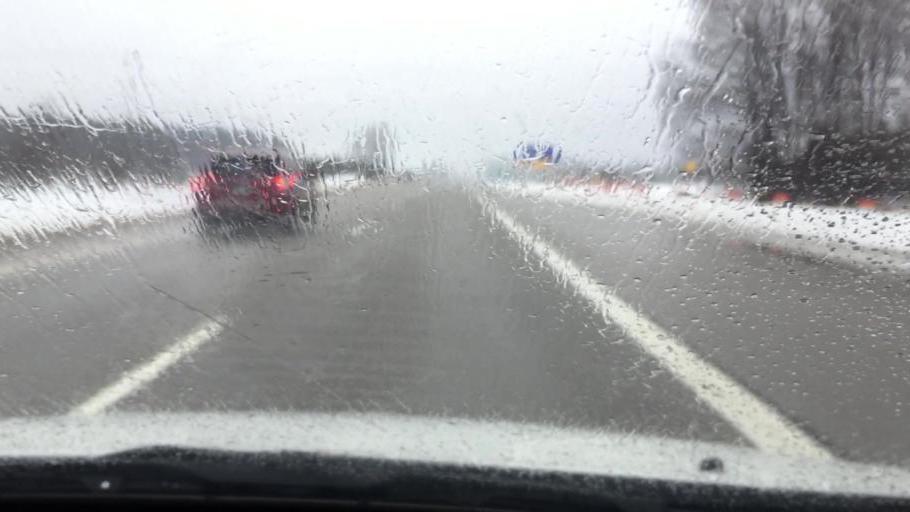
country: US
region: Michigan
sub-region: Wexford County
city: Cadillac
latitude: 44.1259
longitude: -85.4691
